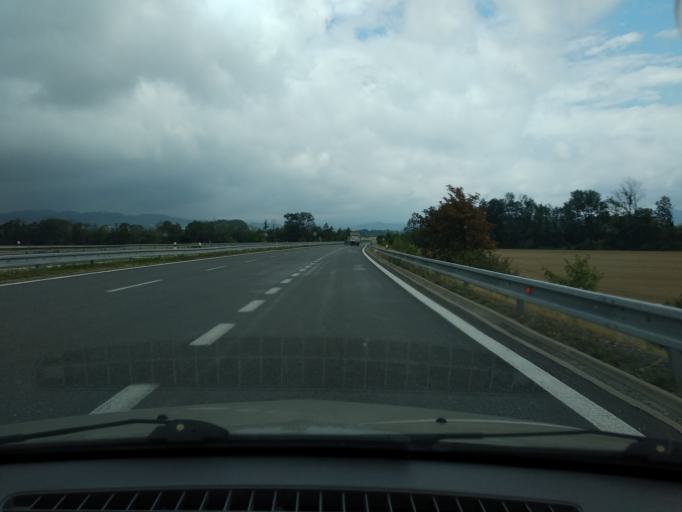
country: CZ
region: Olomoucky
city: Postrelmov
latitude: 49.8963
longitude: 16.8943
